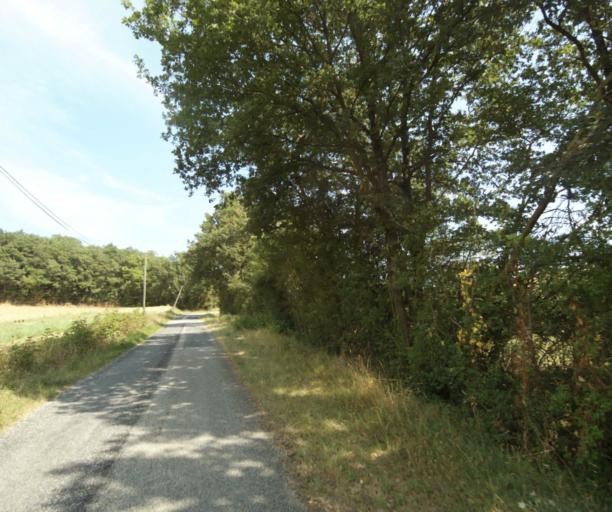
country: FR
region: Midi-Pyrenees
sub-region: Departement de la Haute-Garonne
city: Gaillac-Toulza
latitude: 43.2459
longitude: 1.4121
